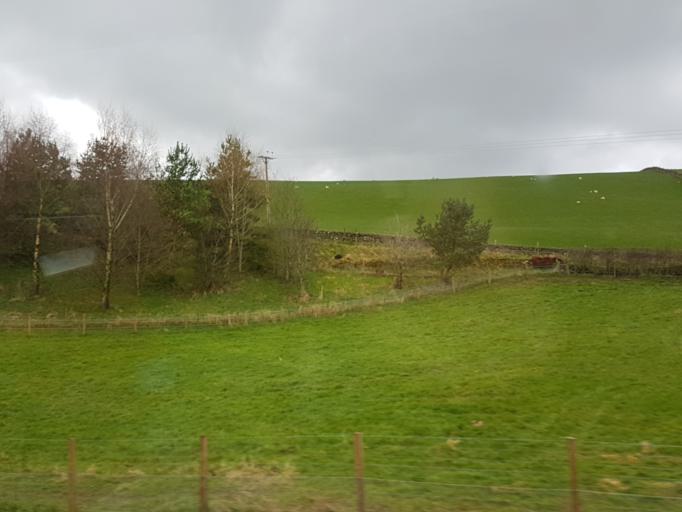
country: GB
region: Scotland
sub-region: The Scottish Borders
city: Galashiels
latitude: 55.6843
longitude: -2.8716
